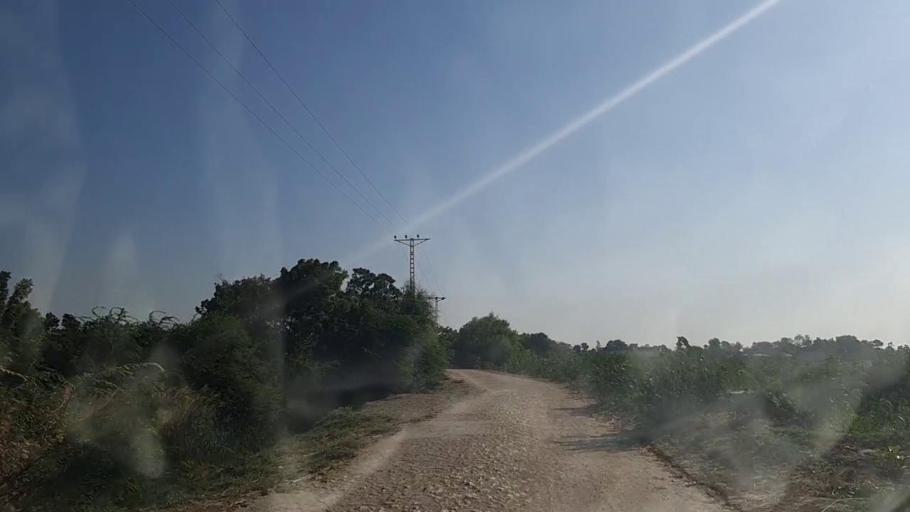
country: PK
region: Sindh
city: Mirpur Batoro
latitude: 24.6168
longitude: 68.1653
